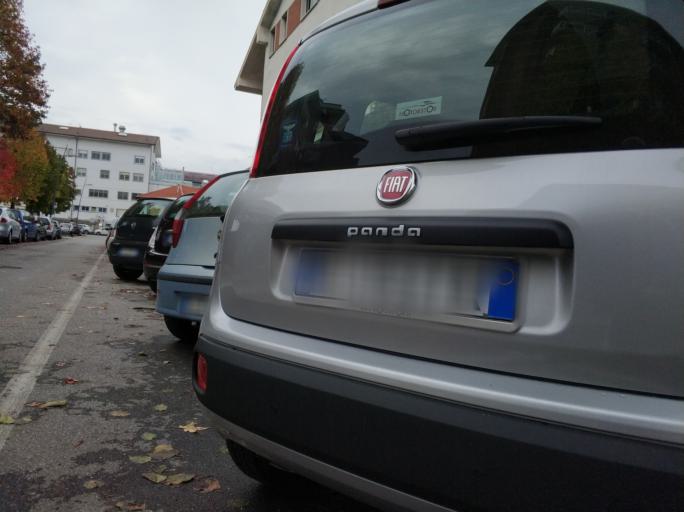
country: IT
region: Piedmont
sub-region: Provincia di Torino
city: Cirie
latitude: 45.2346
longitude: 7.6004
